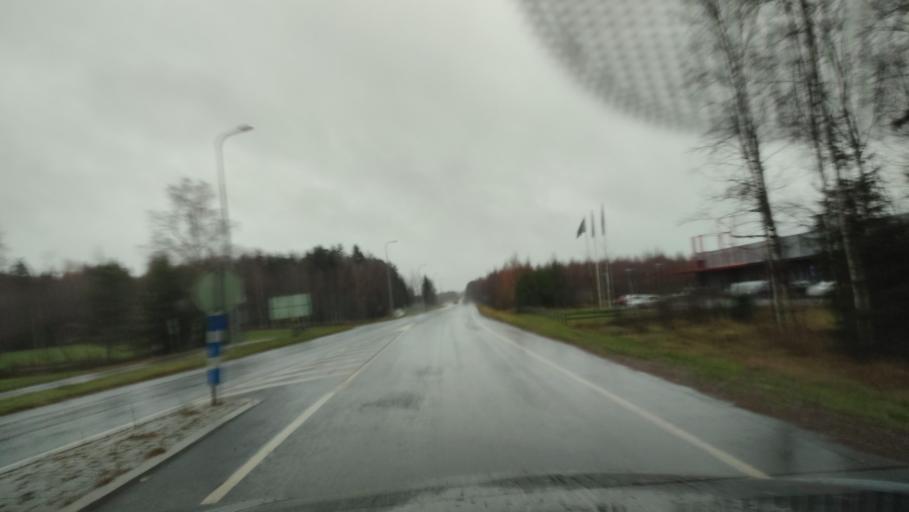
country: FI
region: Ostrobothnia
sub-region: Vaasa
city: Ristinummi
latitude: 63.0518
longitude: 21.7235
